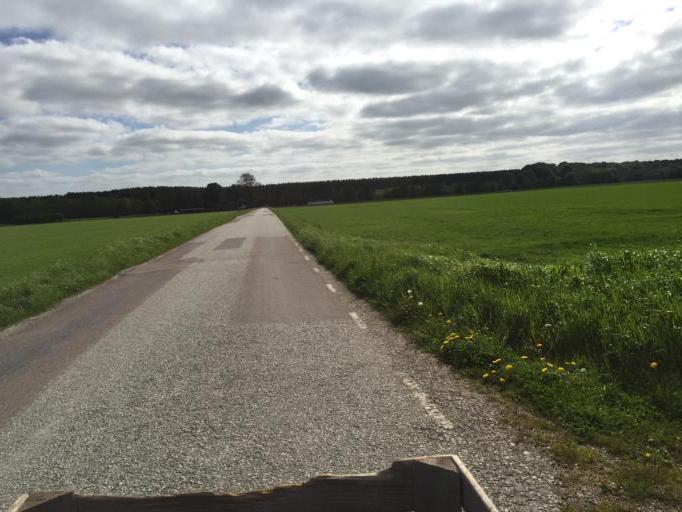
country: SE
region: Skane
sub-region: Sjobo Kommun
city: Blentarp
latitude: 55.6668
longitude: 13.6220
